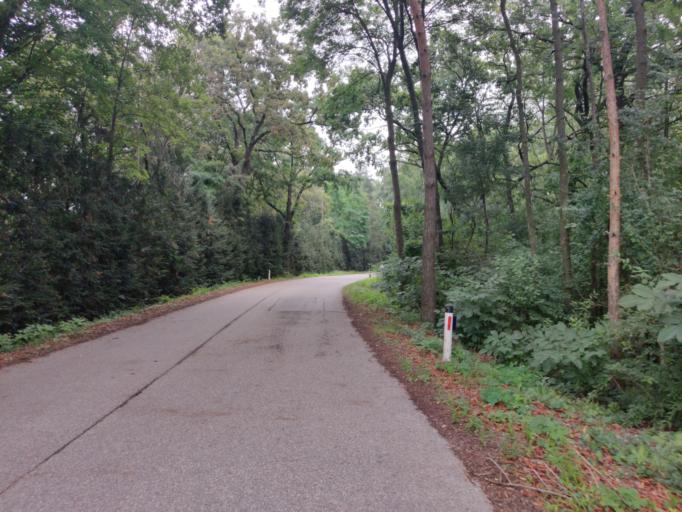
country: AT
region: Lower Austria
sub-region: Politischer Bezirk Tulln
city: Langenrohr
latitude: 48.3295
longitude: 15.9914
